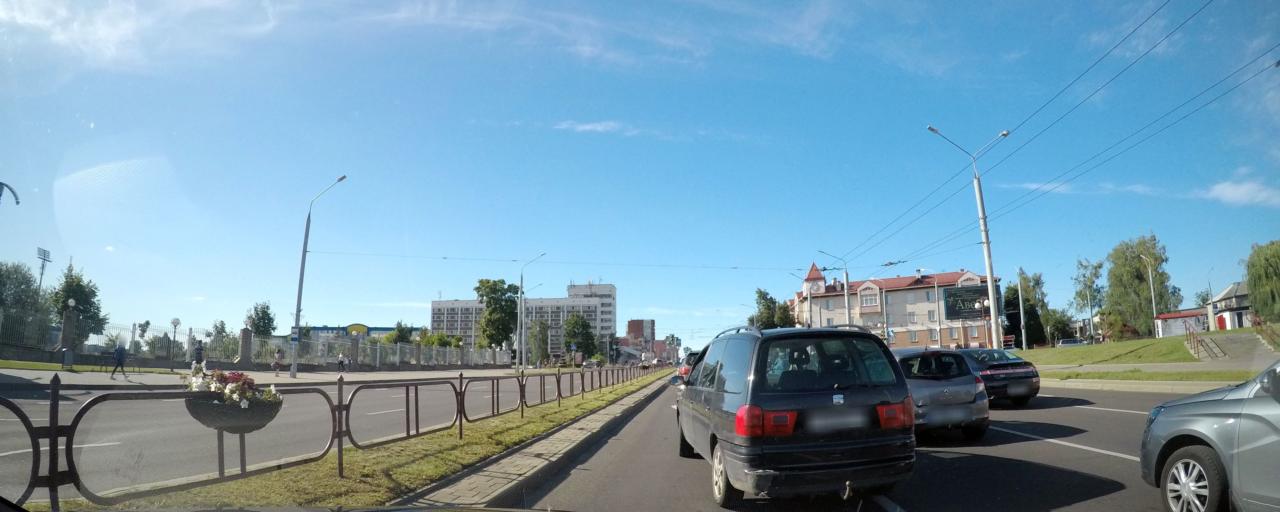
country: BY
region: Grodnenskaya
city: Hrodna
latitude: 53.6894
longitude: 23.8262
